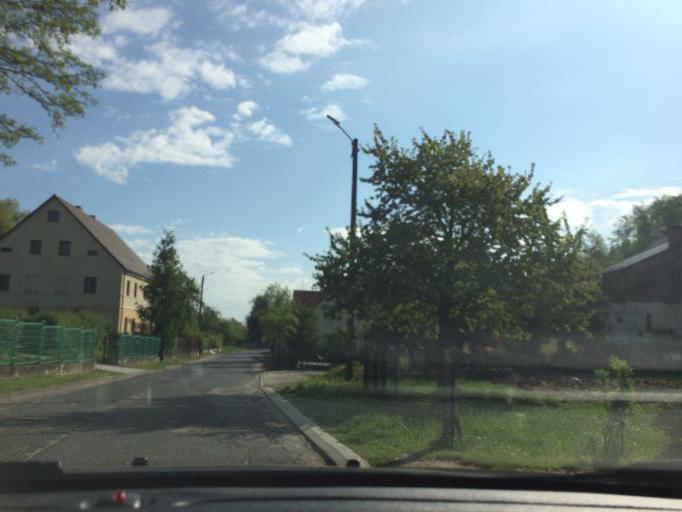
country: PL
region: Lower Silesian Voivodeship
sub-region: Powiat walbrzyski
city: Walim
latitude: 50.7485
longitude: 16.5002
